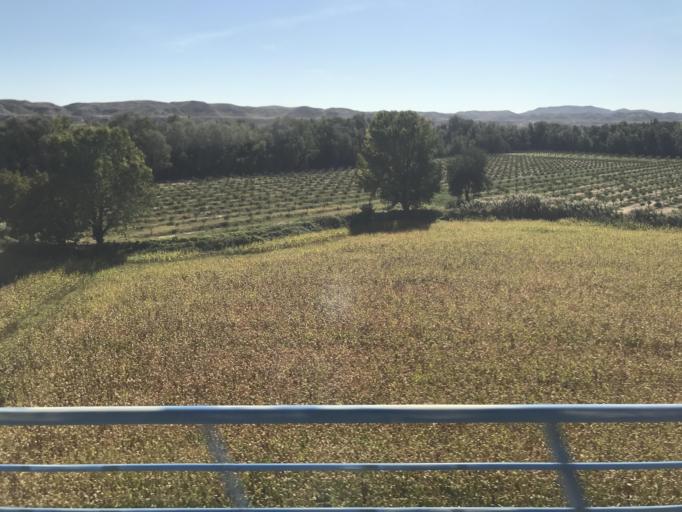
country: ES
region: Aragon
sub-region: Provincia de Zaragoza
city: Plasencia de Jalon
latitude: 41.6935
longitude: -1.2240
